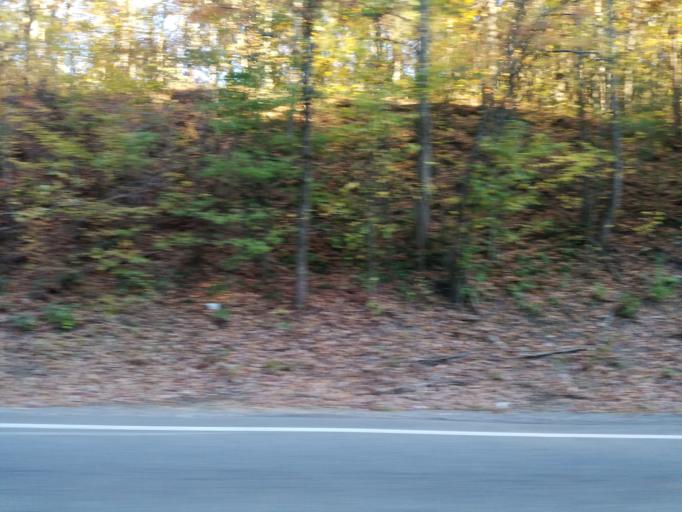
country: US
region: Georgia
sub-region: Pickens County
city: Jasper
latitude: 34.5767
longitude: -84.3022
